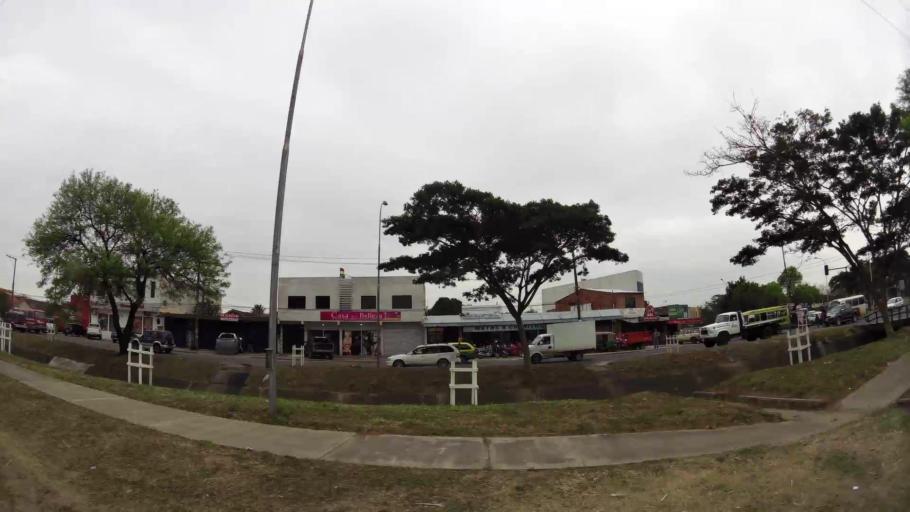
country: BO
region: Santa Cruz
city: Santa Cruz de la Sierra
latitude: -17.7806
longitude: -63.1474
